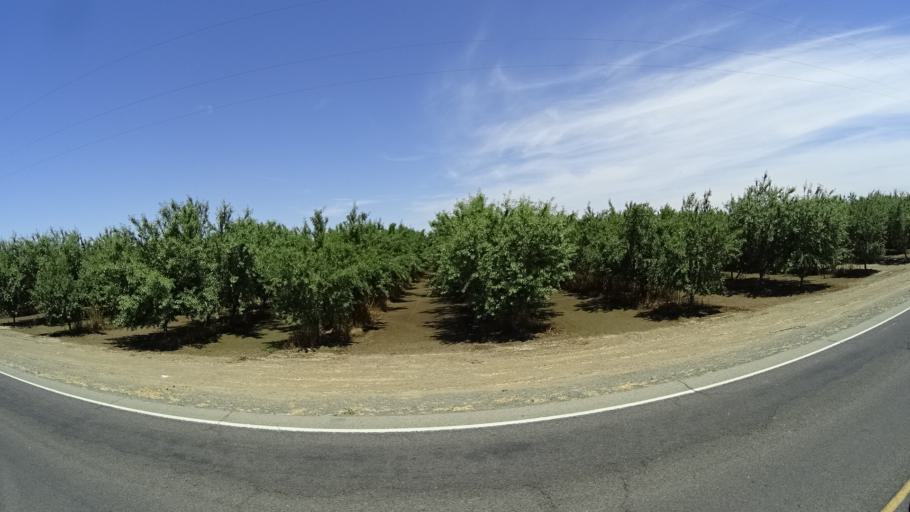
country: US
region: California
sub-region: Kings County
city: Lemoore
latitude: 36.3425
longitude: -119.7737
